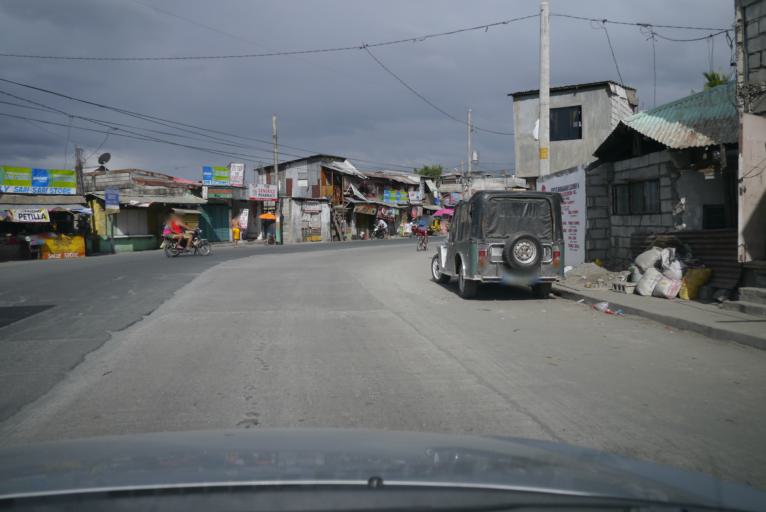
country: PH
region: Calabarzon
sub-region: Province of Rizal
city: Taytay
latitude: 14.5441
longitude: 121.1246
